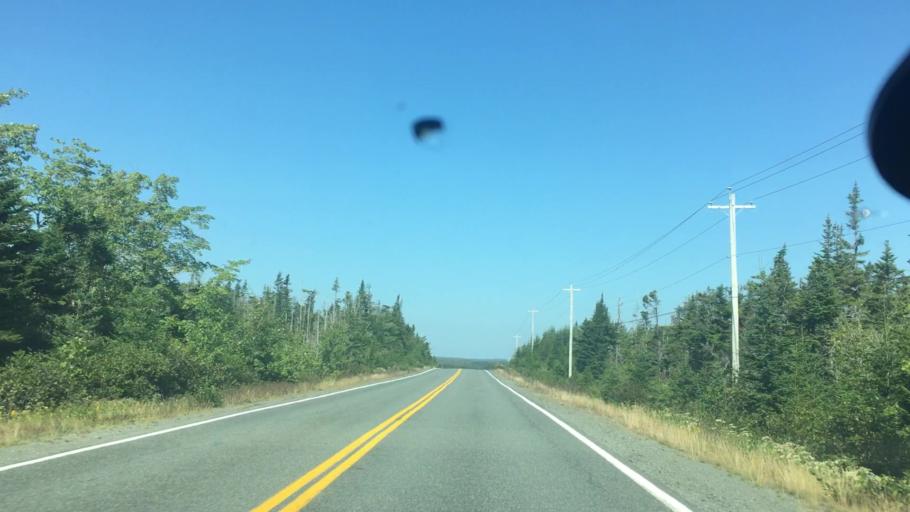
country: CA
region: Nova Scotia
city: Antigonish
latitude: 44.9906
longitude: -62.0960
